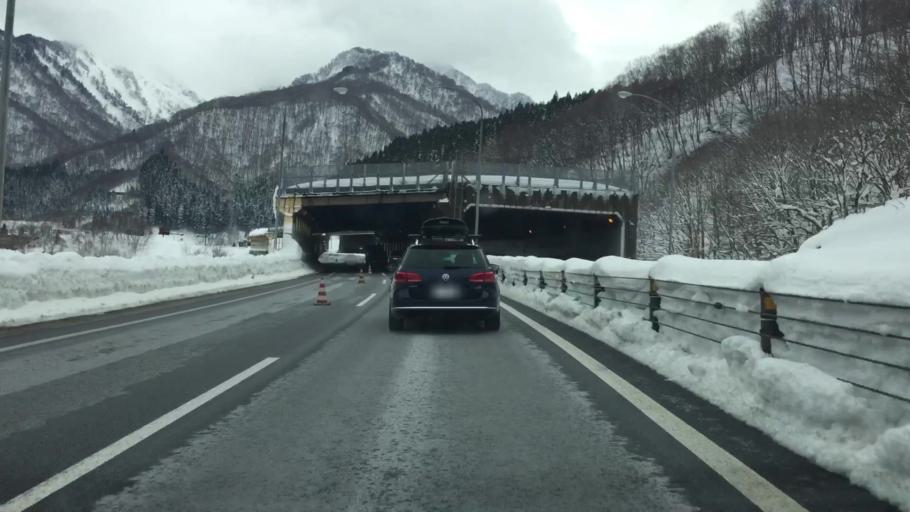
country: JP
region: Niigata
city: Shiozawa
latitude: 36.8685
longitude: 138.8675
